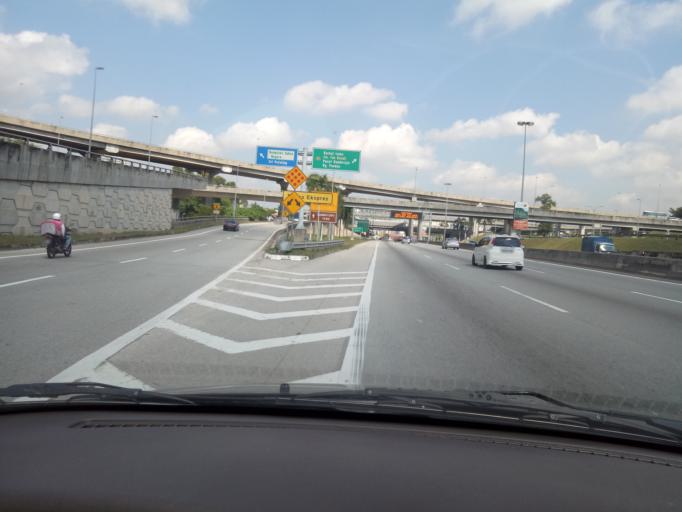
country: MY
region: Selangor
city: Kampong Baharu Balakong
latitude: 3.0627
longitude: 101.6864
